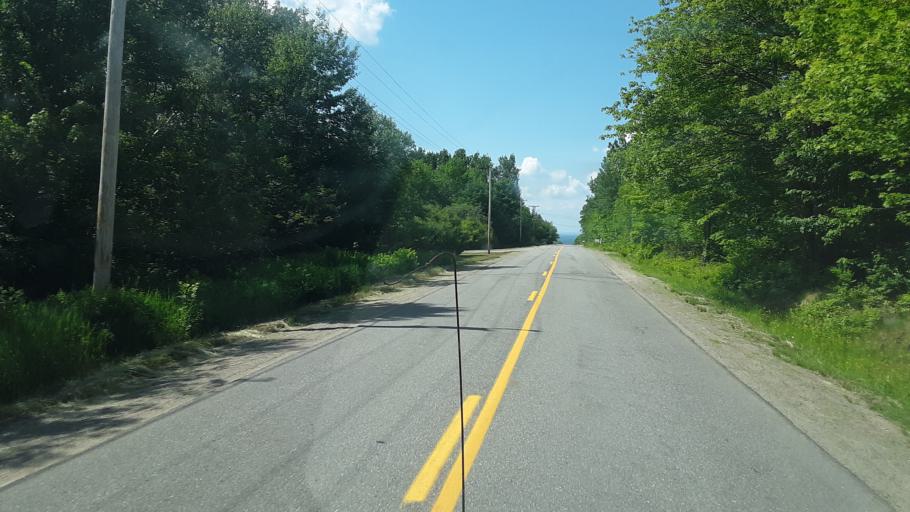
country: US
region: Maine
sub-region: Washington County
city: Calais
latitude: 45.0906
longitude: -67.5049
